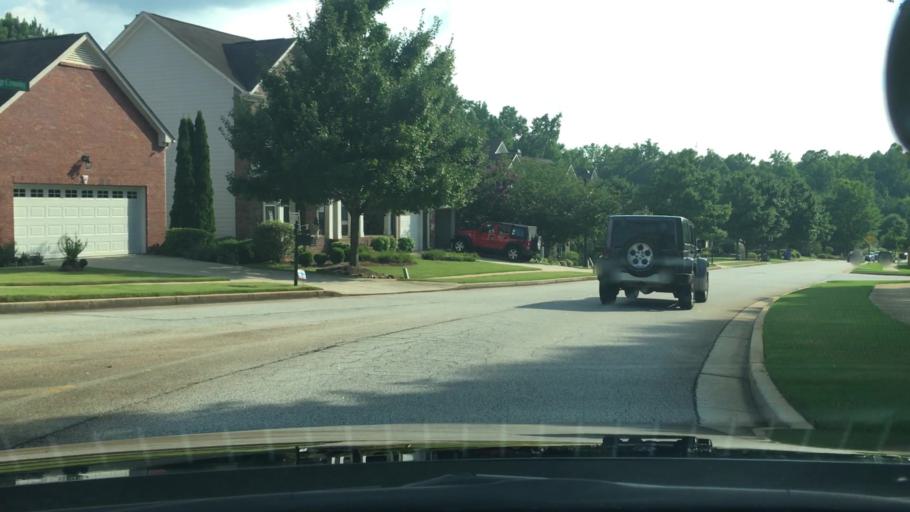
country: US
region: Georgia
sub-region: Coweta County
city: East Newnan
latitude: 33.3820
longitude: -84.7430
